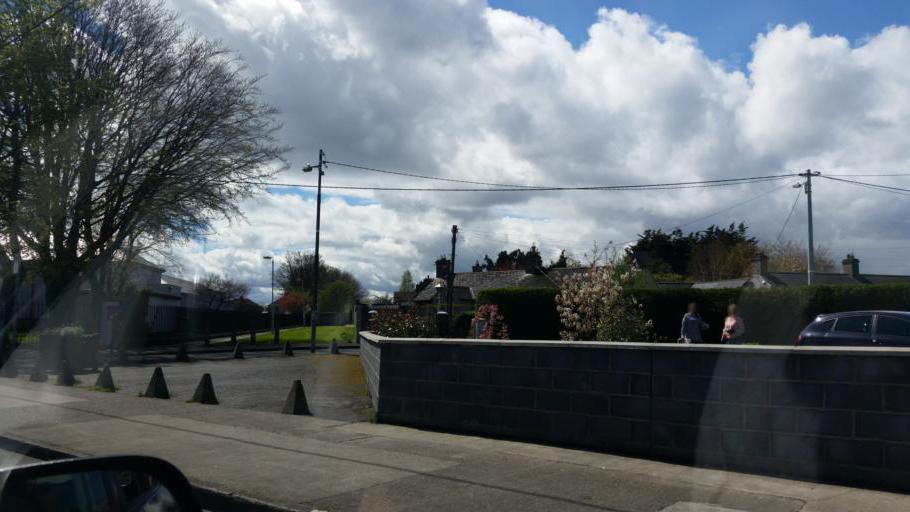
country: IE
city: Killester
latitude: 53.3796
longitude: -6.2050
